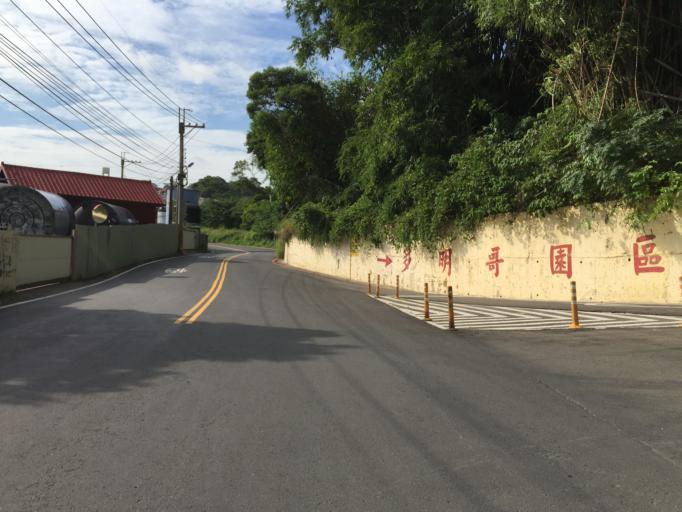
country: TW
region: Taiwan
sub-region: Hsinchu
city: Hsinchu
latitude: 24.7743
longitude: 120.9330
